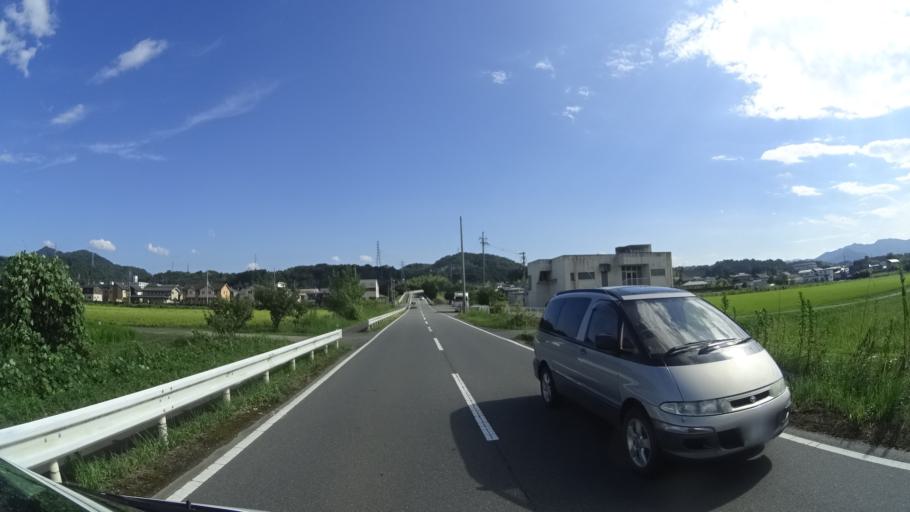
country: JP
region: Kyoto
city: Fukuchiyama
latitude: 35.3026
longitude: 135.1707
